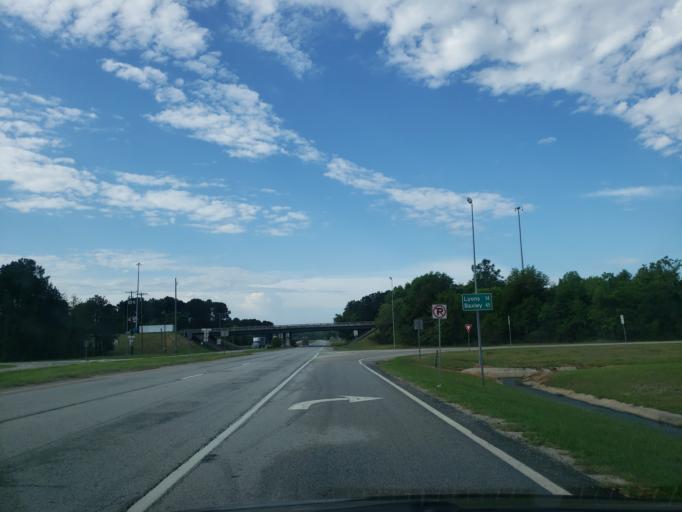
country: US
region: Georgia
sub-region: Emanuel County
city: Swainsboro
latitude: 32.4026
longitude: -82.3068
